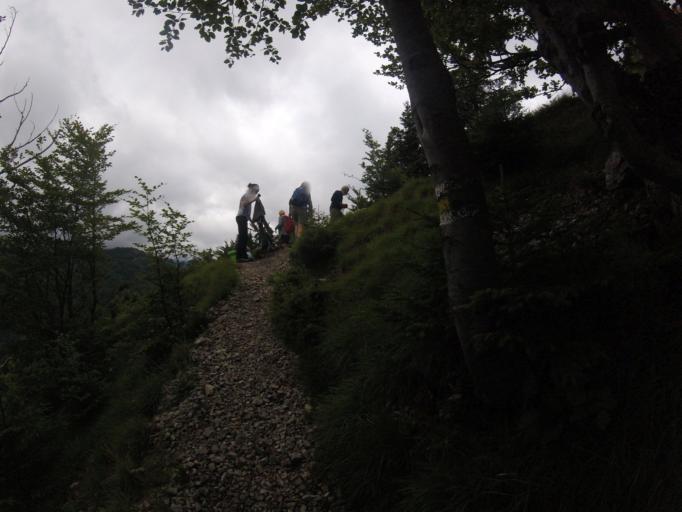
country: SK
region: Zilinsky
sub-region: Okres Zilina
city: Terchova
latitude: 49.2359
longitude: 19.0150
